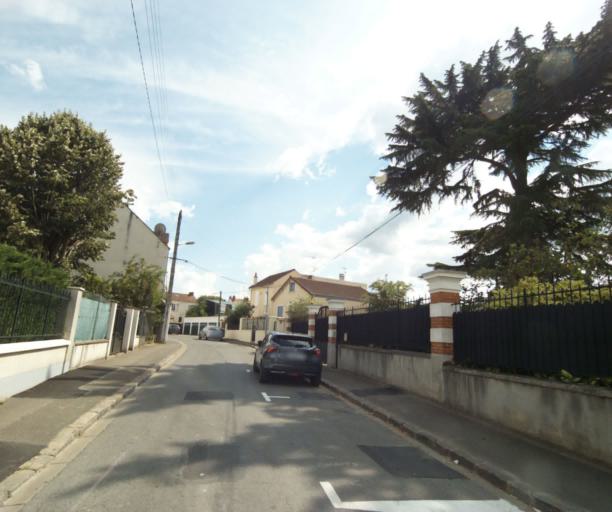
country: FR
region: Ile-de-France
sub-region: Departement de Seine-et-Marne
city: Avon
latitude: 48.4045
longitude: 2.7249
